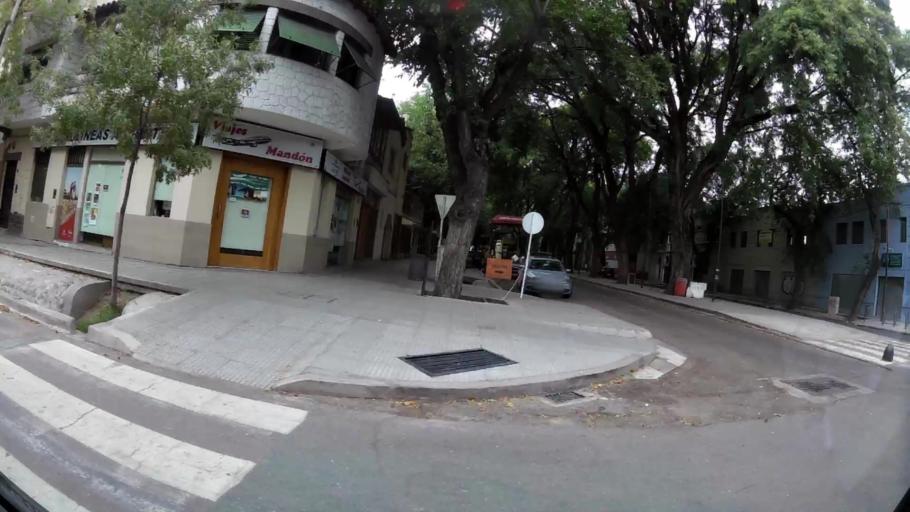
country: AR
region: Mendoza
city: Mendoza
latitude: -32.8866
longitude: -68.8437
